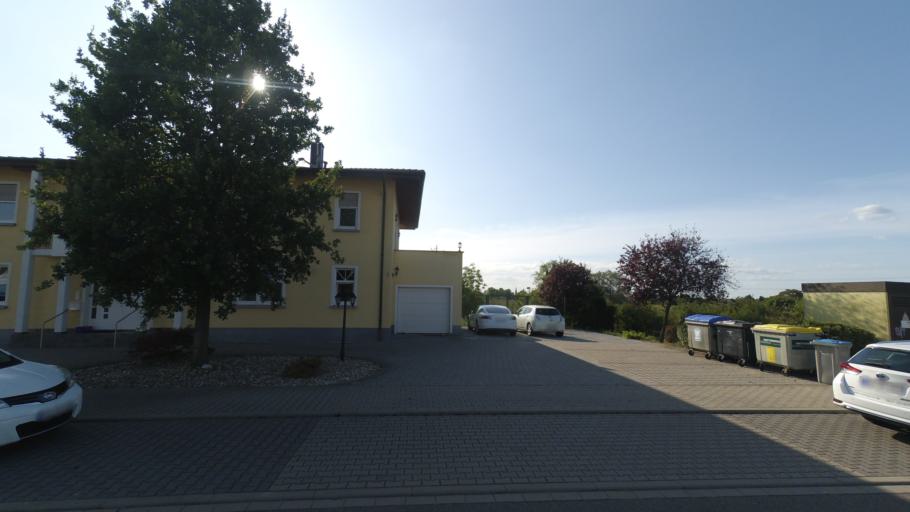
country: DE
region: Baden-Wuerttemberg
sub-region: Karlsruhe Region
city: Mannheim
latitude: 49.5430
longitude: 8.4661
